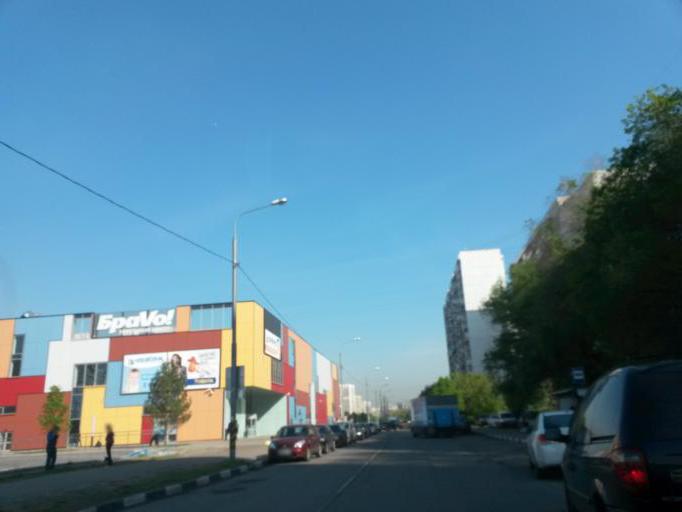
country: RU
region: Moscow
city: Brateyevo
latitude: 55.6385
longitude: 37.7609
